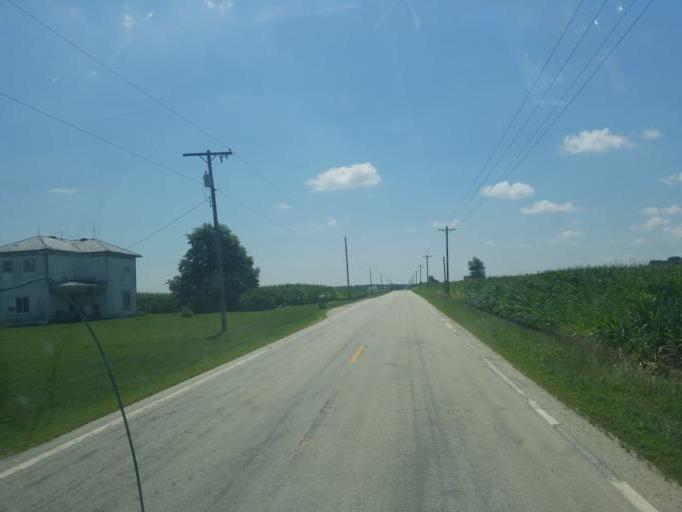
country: US
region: Ohio
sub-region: Allen County
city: Spencerville
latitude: 40.6898
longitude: -84.4256
